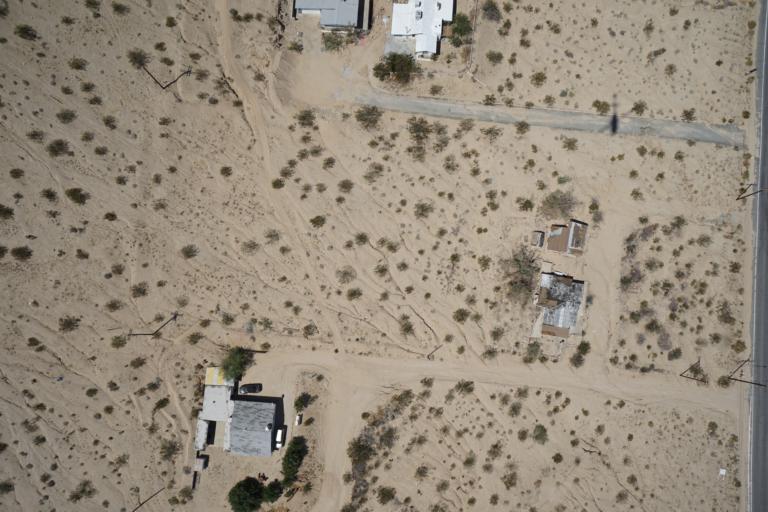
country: US
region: California
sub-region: San Bernardino County
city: Twentynine Palms
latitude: 34.1347
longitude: -116.0660
